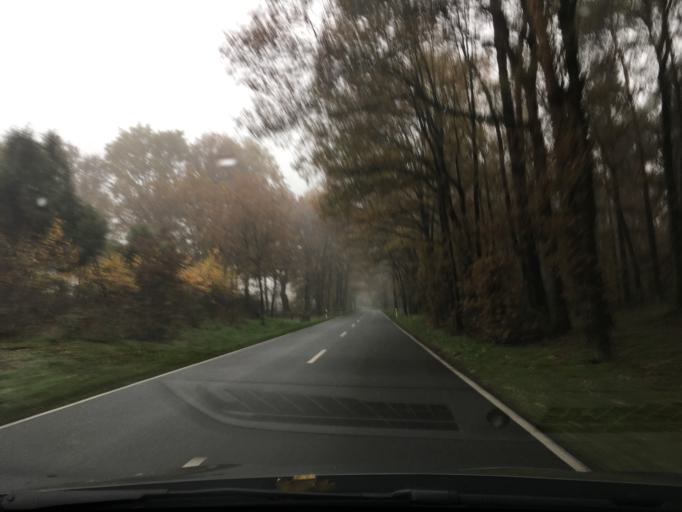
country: DE
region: North Rhine-Westphalia
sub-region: Regierungsbezirk Munster
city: Ahaus
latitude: 52.0993
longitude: 6.9139
